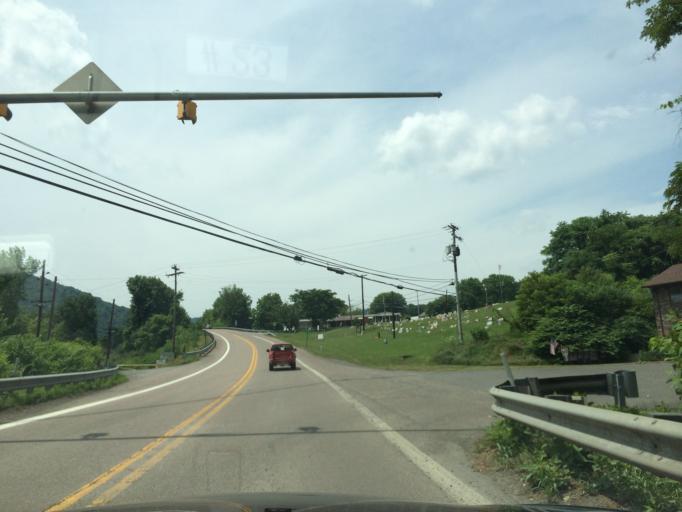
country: US
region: Maryland
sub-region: Allegany County
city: Westernport
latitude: 39.4808
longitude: -79.0681
